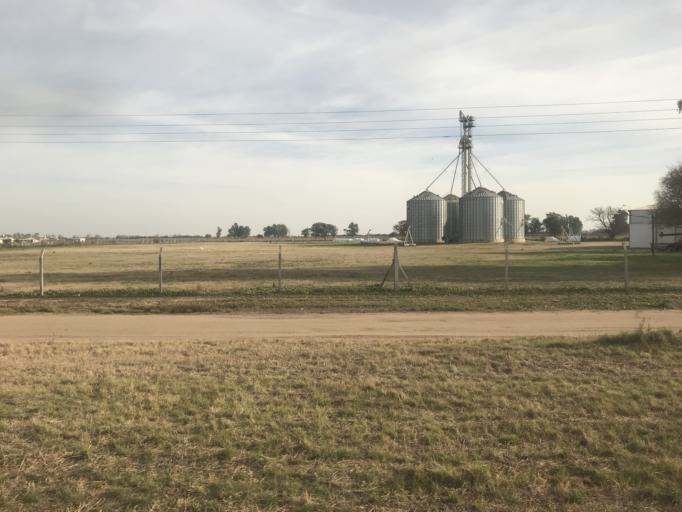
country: AR
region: Cordoba
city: Pilar
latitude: -31.6726
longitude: -63.8940
